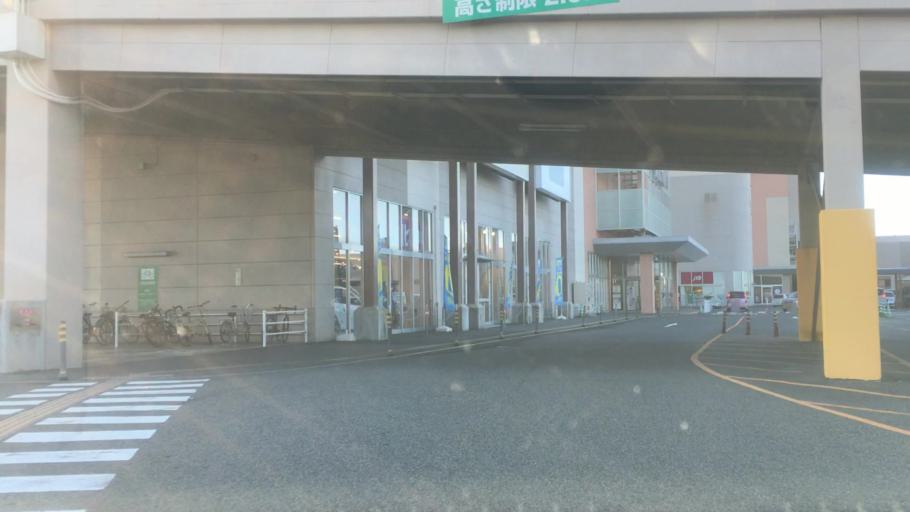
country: JP
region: Tottori
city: Tottori
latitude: 35.5226
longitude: 134.2015
